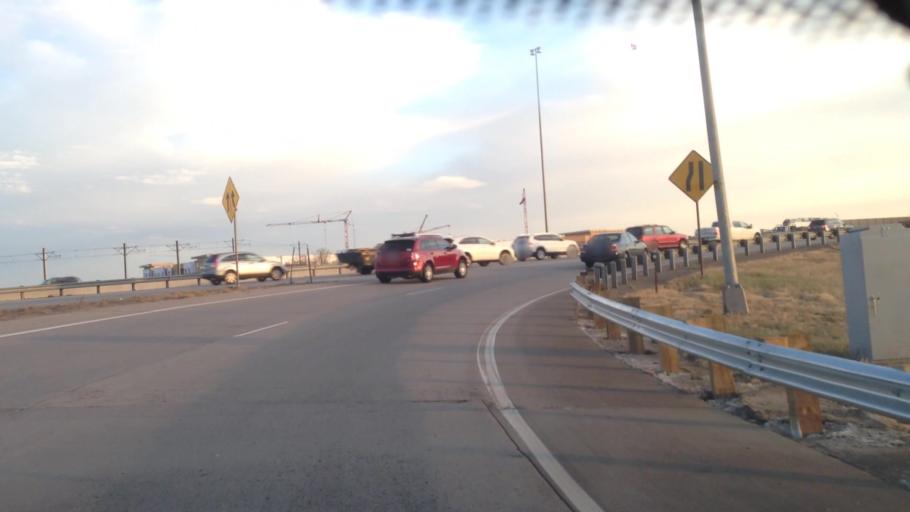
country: US
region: Colorado
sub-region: Adams County
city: Aurora
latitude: 39.6759
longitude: -104.8293
